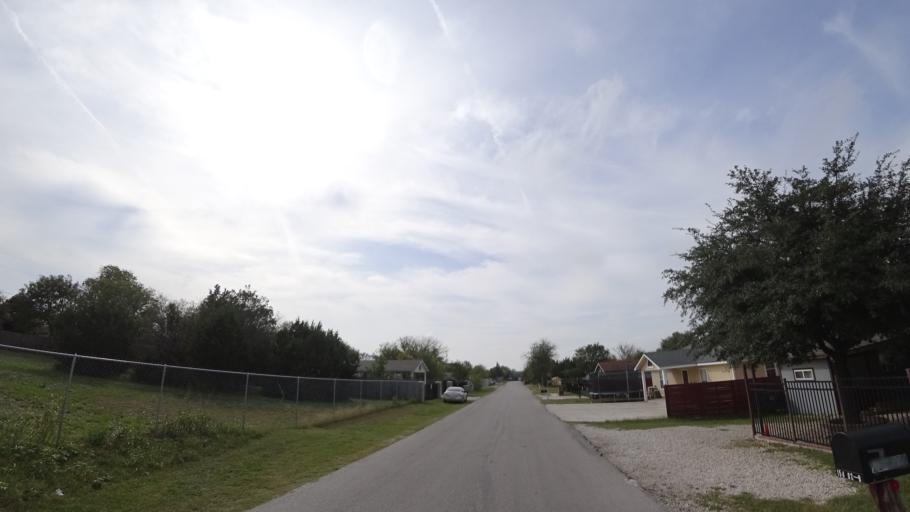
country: US
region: Texas
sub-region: Travis County
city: Wells Branch
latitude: 30.4513
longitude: -97.6710
